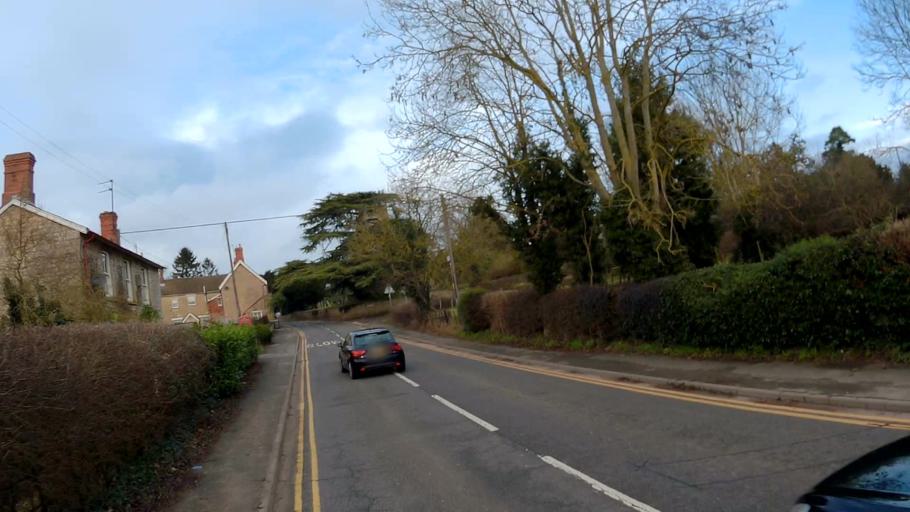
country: GB
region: England
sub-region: Lincolnshire
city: Bourne
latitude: 52.7822
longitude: -0.4266
